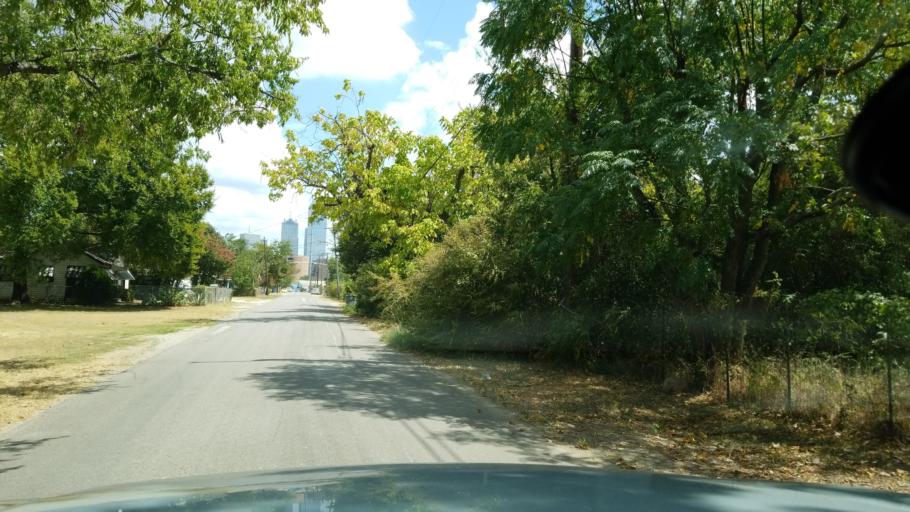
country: US
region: Texas
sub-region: Dallas County
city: Dallas
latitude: 32.7755
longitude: -96.8281
